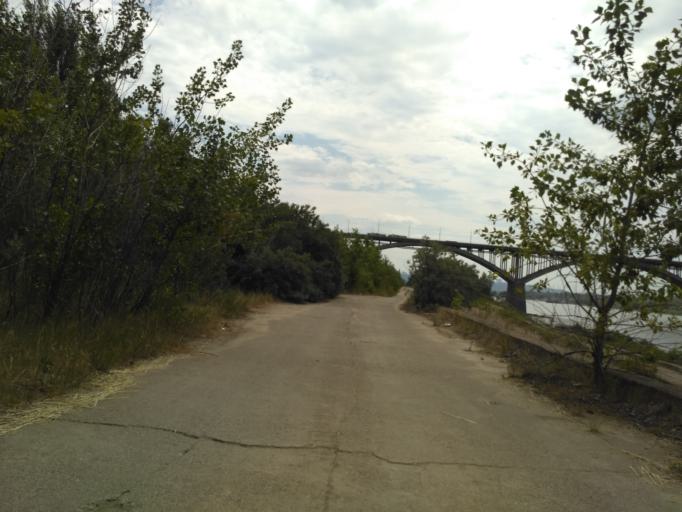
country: RU
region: Nizjnij Novgorod
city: Nizhniy Novgorod
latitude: 56.3028
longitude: 43.9676
